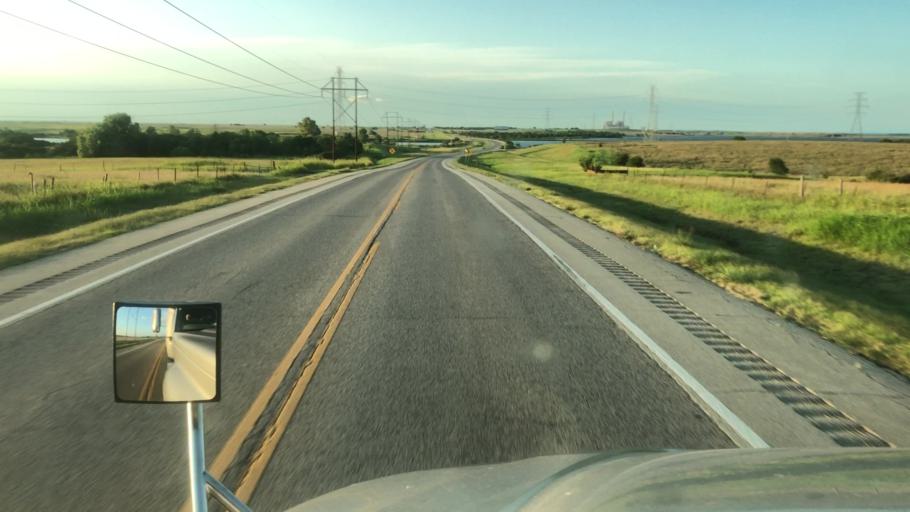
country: US
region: Oklahoma
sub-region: Noble County
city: Perry
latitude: 36.3977
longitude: -97.0676
